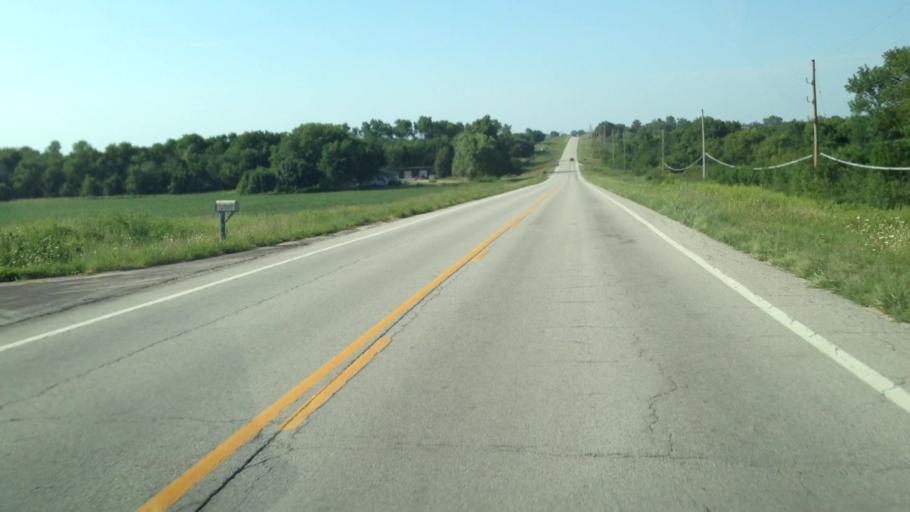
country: US
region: Kansas
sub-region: Allen County
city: Iola
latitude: 37.9900
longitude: -95.1705
